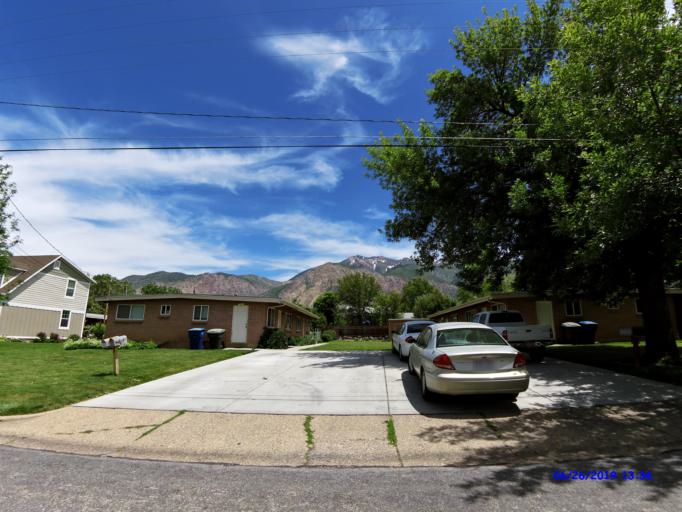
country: US
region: Utah
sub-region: Weber County
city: South Ogden
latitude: 41.2049
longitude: -111.9597
